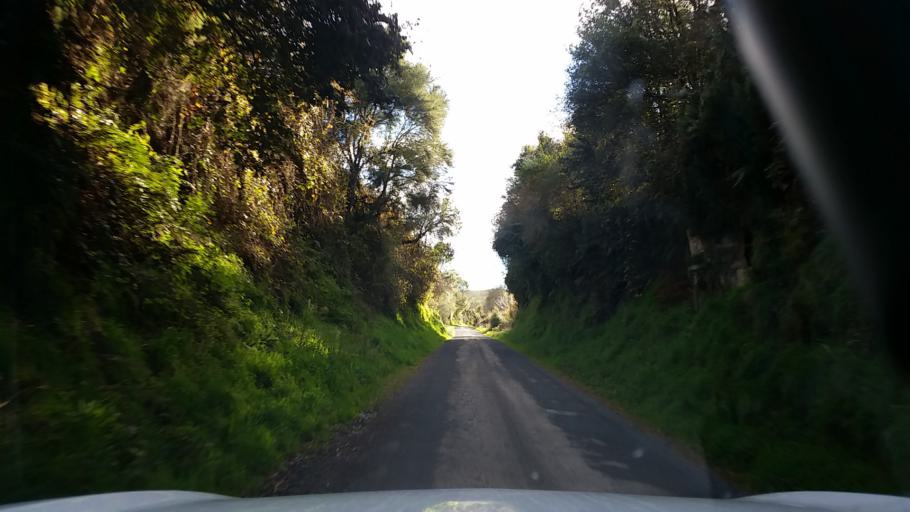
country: NZ
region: Waikato
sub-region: South Waikato District
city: Tokoroa
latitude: -38.3881
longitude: 176.0780
